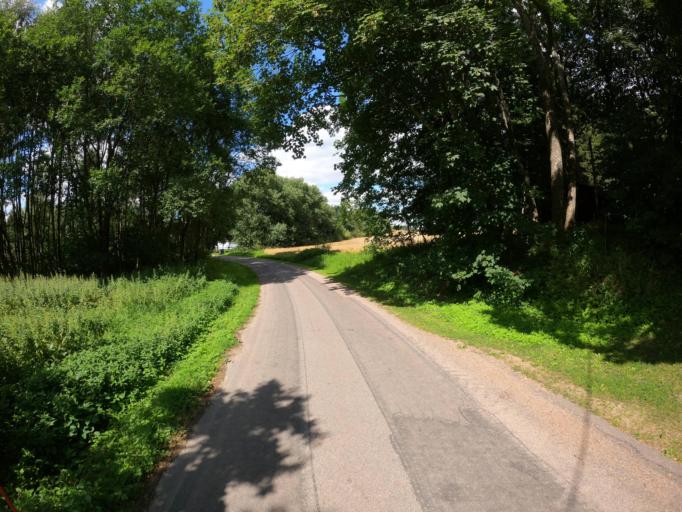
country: SE
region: Skane
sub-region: Lunds Kommun
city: Veberod
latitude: 55.5894
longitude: 13.4871
